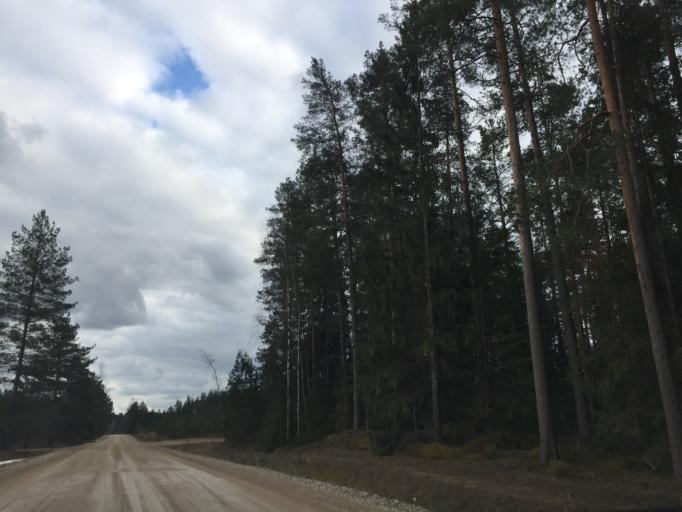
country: LV
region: Ogre
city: Jumprava
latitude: 56.5915
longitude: 24.9885
